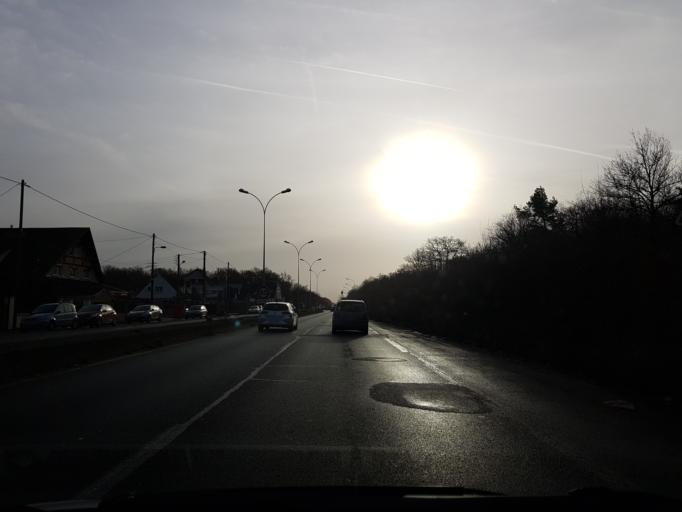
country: FR
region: Ile-de-France
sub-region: Departement de l'Essonne
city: Brunoy
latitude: 48.6798
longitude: 2.4943
